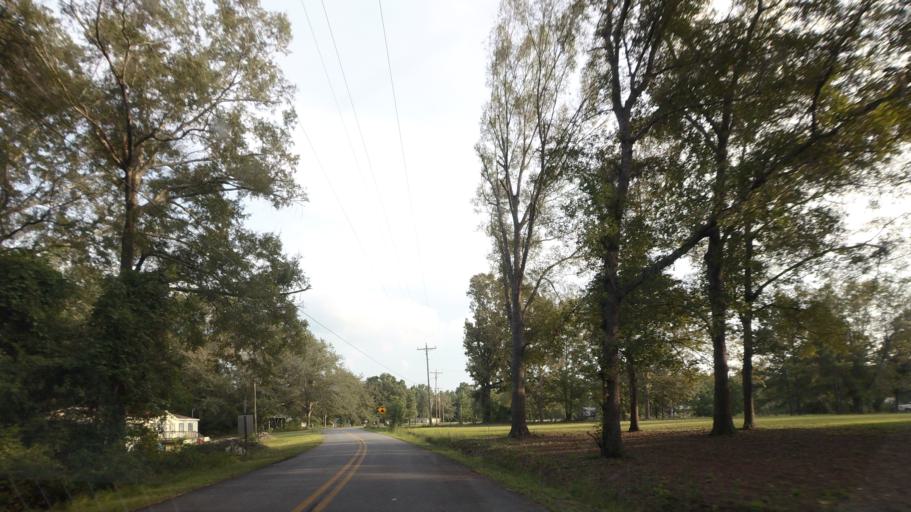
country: US
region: Georgia
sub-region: Wilkinson County
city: Gordon
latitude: 32.8270
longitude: -83.3909
